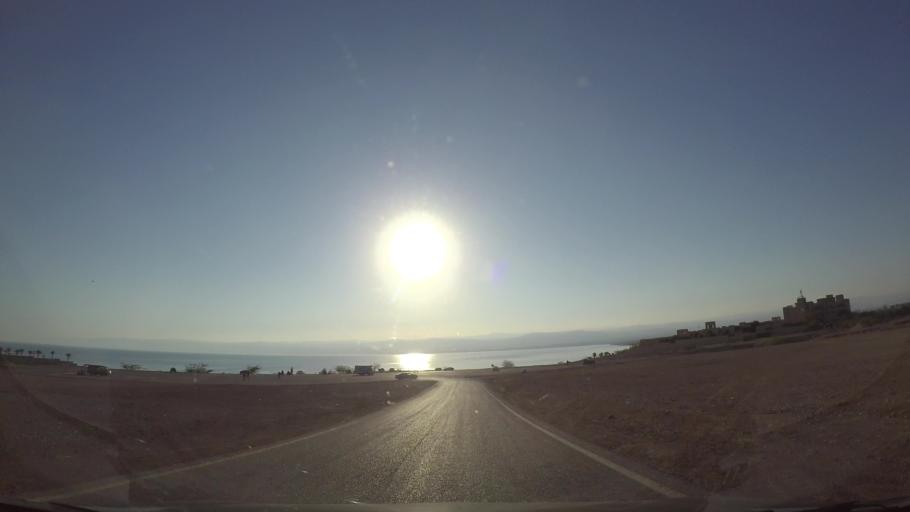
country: PS
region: West Bank
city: Jericho
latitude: 31.7494
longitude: 35.5935
